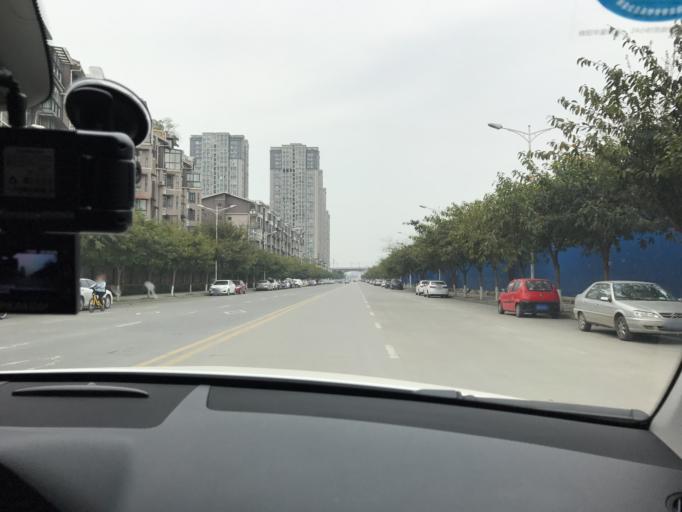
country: CN
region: Sichuan
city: Mianyang
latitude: 31.4587
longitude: 104.6899
